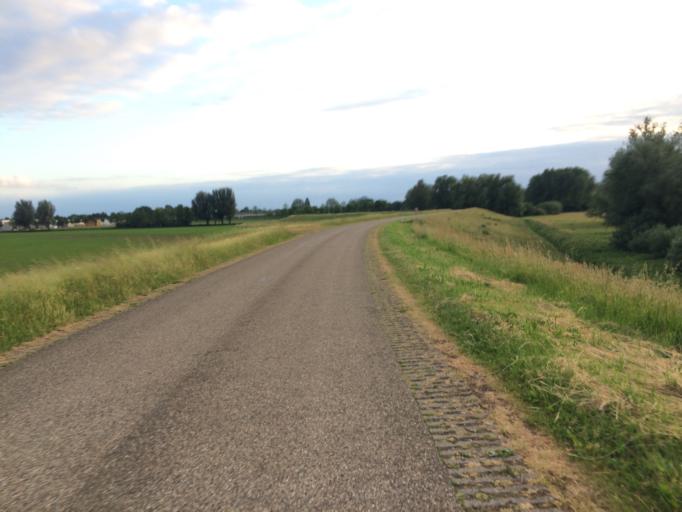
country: NL
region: North Brabant
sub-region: Gemeente 's-Hertogenbosch
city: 's-Hertogenbosch
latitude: 51.7375
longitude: 5.3191
